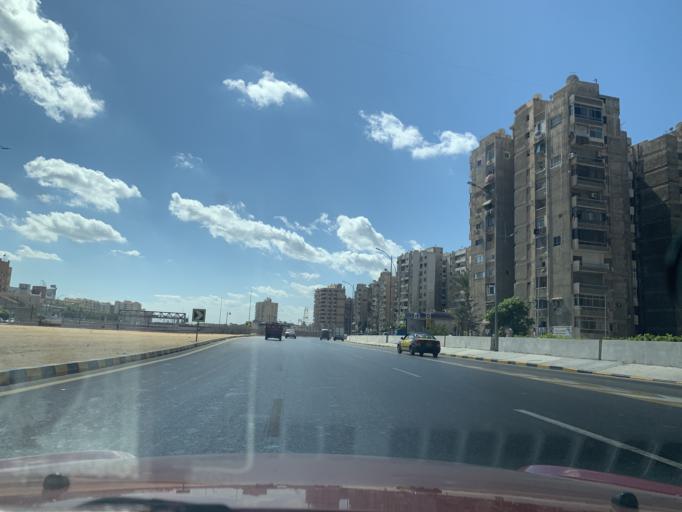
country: EG
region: Alexandria
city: Alexandria
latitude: 31.2102
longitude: 29.9568
